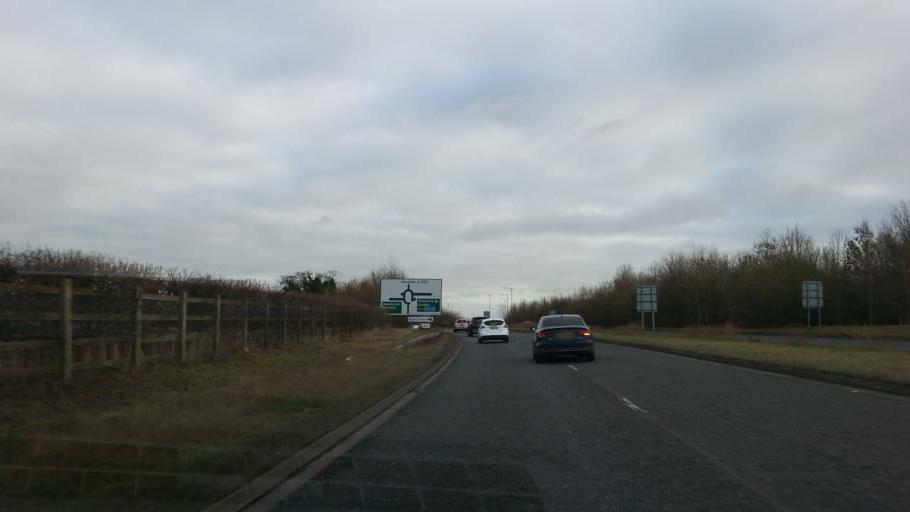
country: GB
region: England
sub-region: Cambridgeshire
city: Sawston
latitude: 52.1306
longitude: 0.2188
